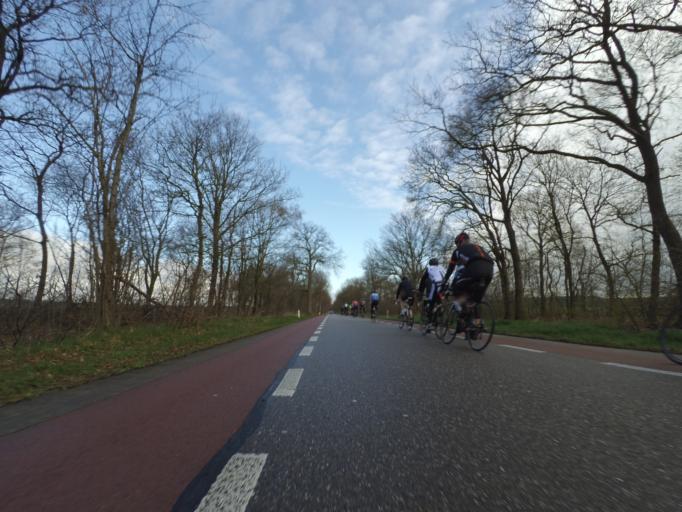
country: NL
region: Gelderland
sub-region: Gemeente Arnhem
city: Hoogkamp
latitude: 52.0876
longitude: 5.8793
